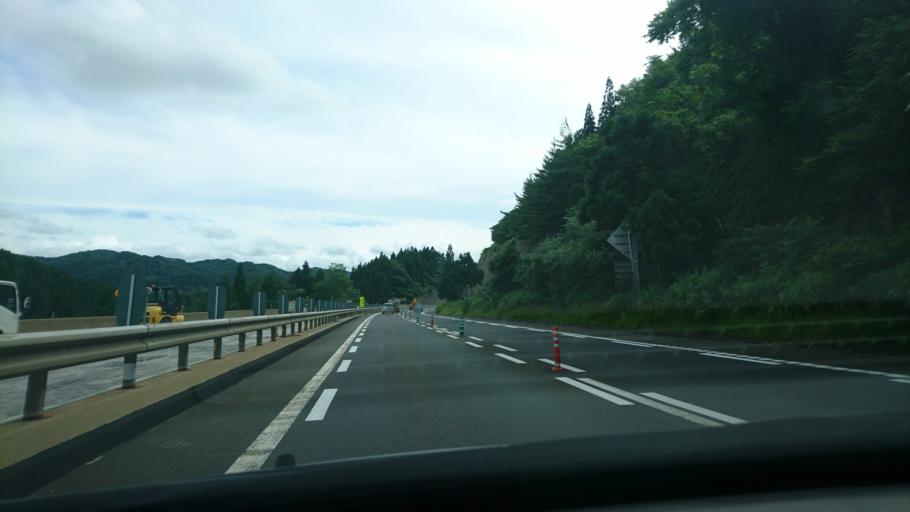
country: JP
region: Iwate
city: Ichinohe
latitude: 40.2232
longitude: 141.3614
